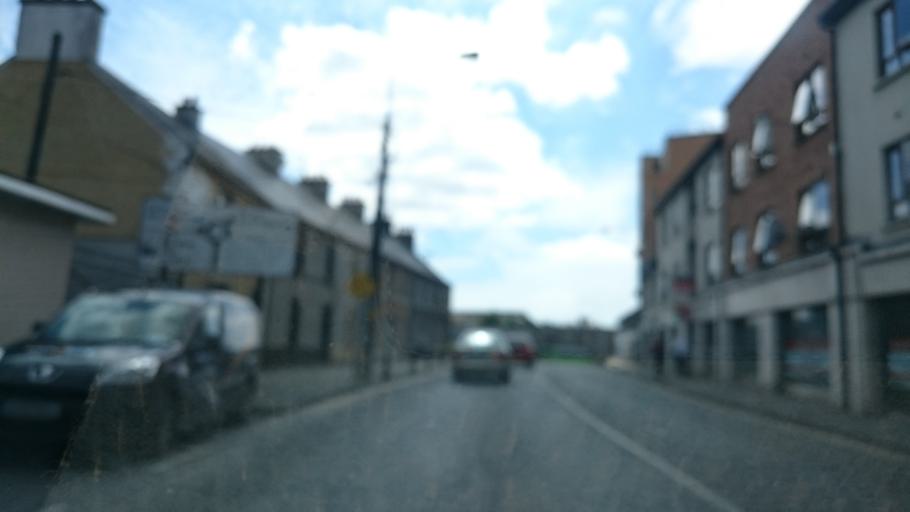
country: IE
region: Leinster
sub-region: Kilkenny
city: Kilkenny
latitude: 52.6567
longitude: -7.2456
